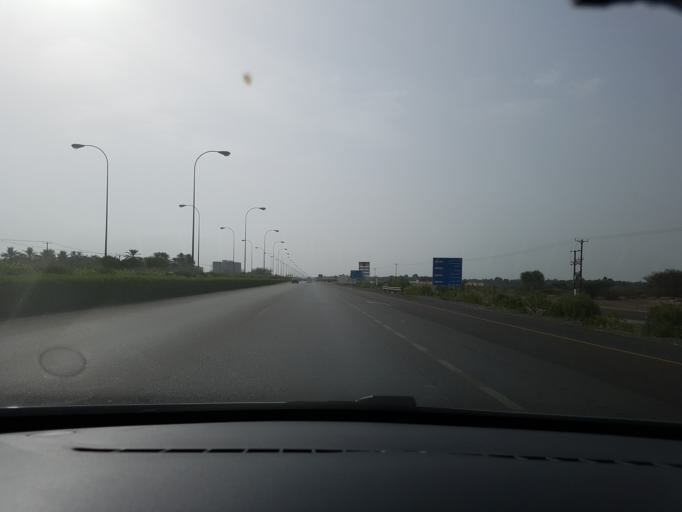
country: OM
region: Al Batinah
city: Al Sohar
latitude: 24.4079
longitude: 56.6492
